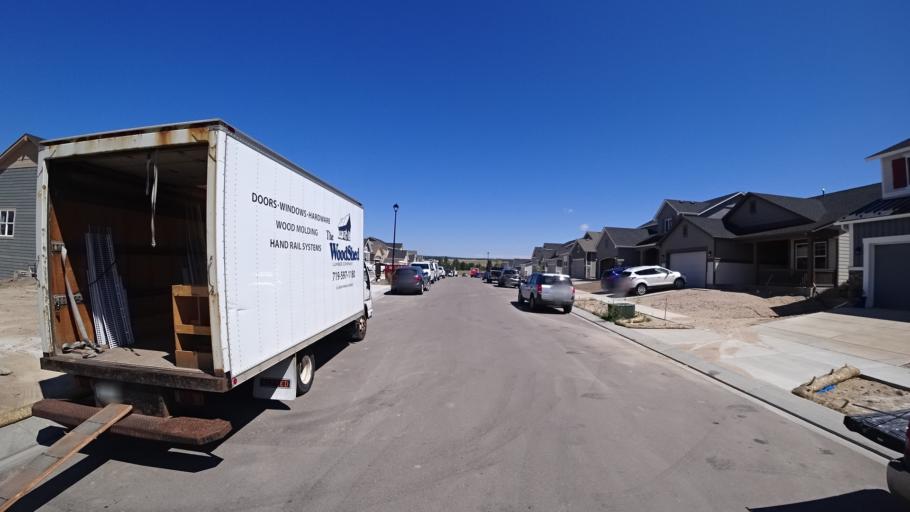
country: US
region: Colorado
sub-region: El Paso County
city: Black Forest
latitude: 38.9931
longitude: -104.7703
